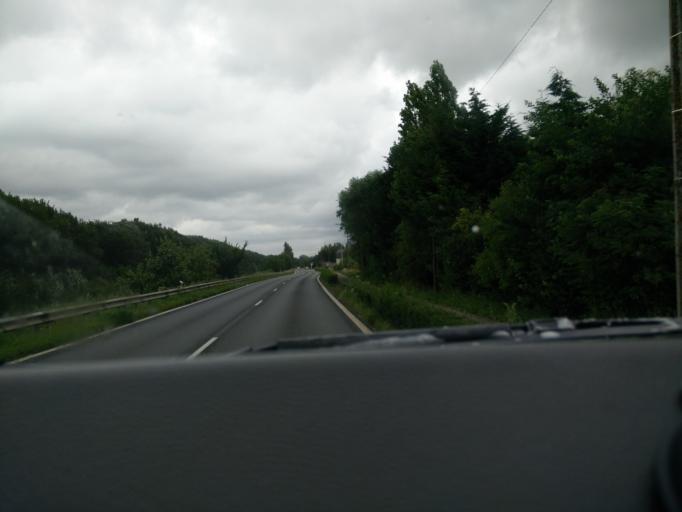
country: FR
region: Nord-Pas-de-Calais
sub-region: Departement du Nord
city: Bierne
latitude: 50.9789
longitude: 2.4155
